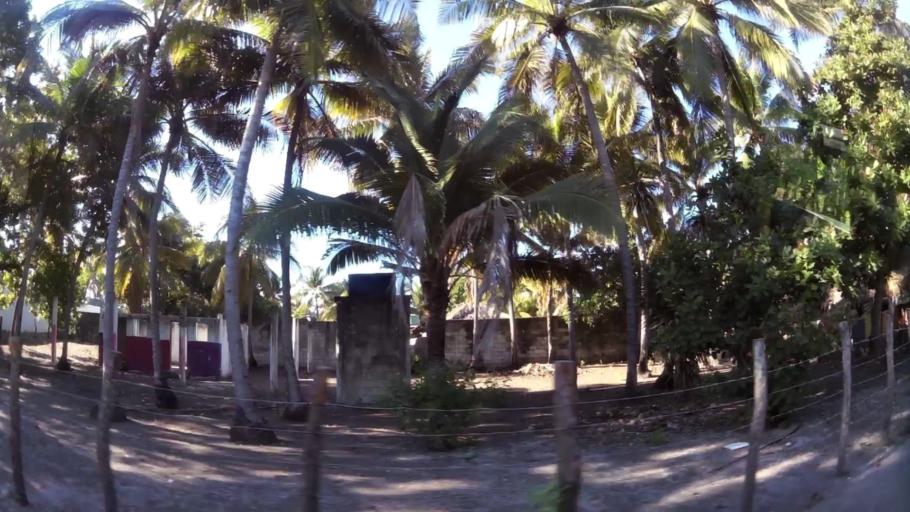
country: GT
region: Santa Rosa
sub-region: Municipio de Taxisco
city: Taxisco
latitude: 13.8895
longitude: -90.4798
